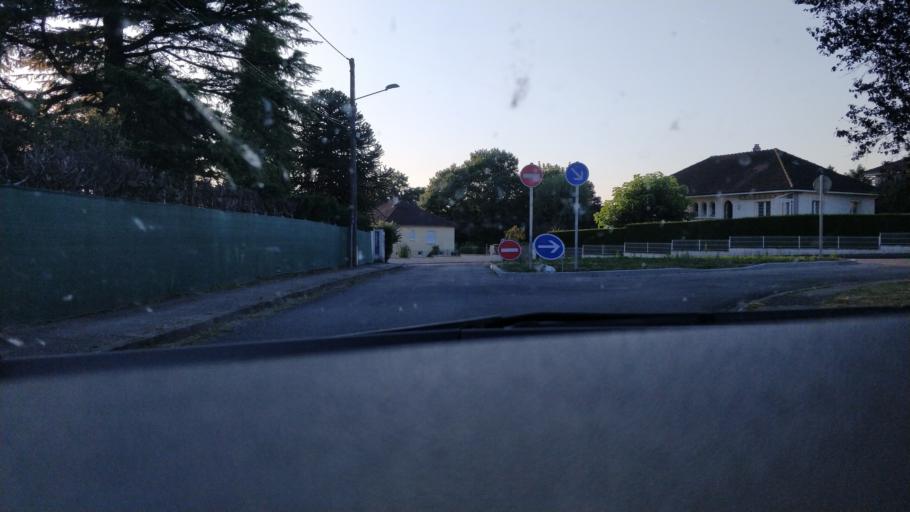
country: FR
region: Limousin
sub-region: Departement de la Haute-Vienne
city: Couzeix
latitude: 45.8839
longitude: 1.2401
